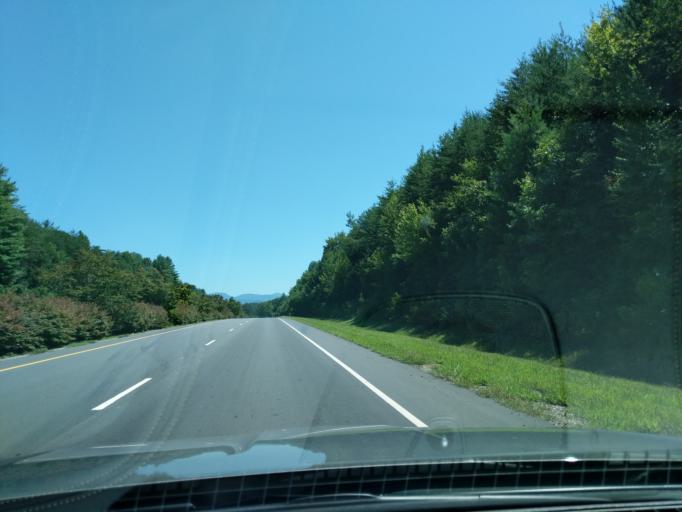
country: US
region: North Carolina
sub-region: Macon County
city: Franklin
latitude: 35.1645
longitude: -83.4224
